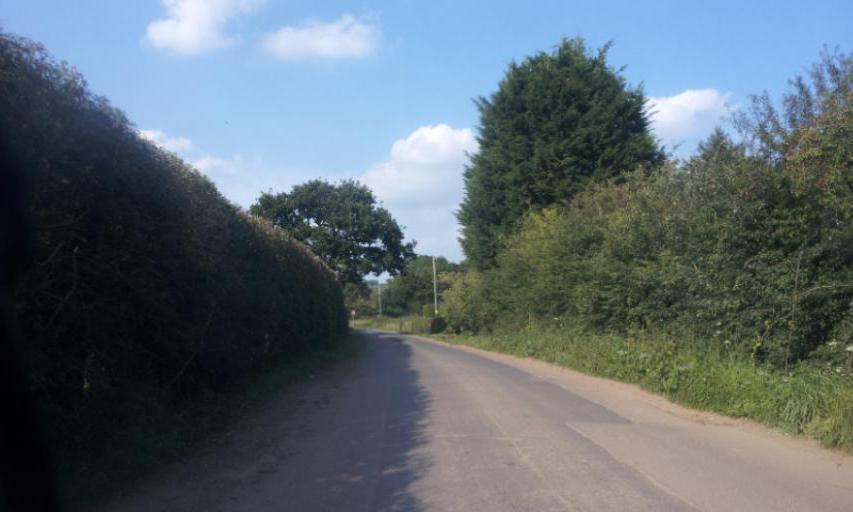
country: GB
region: England
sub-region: Kent
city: Yalding
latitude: 51.2175
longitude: 0.4379
